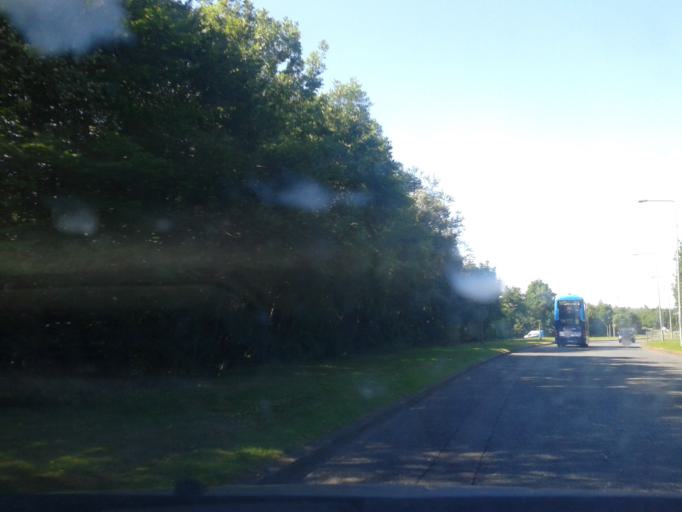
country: IE
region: Leinster
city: Hartstown
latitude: 53.4140
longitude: -6.4227
